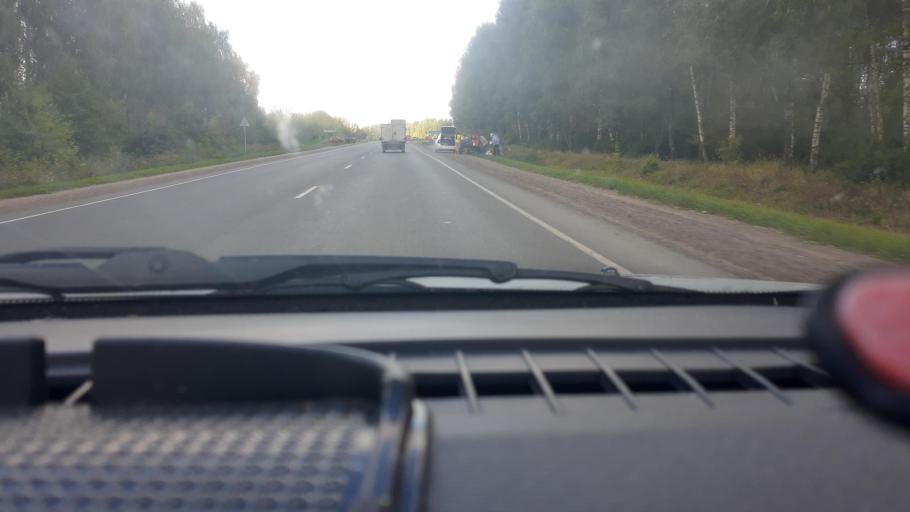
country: RU
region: Nizjnij Novgorod
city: Arzamas
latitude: 55.2923
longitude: 43.9416
